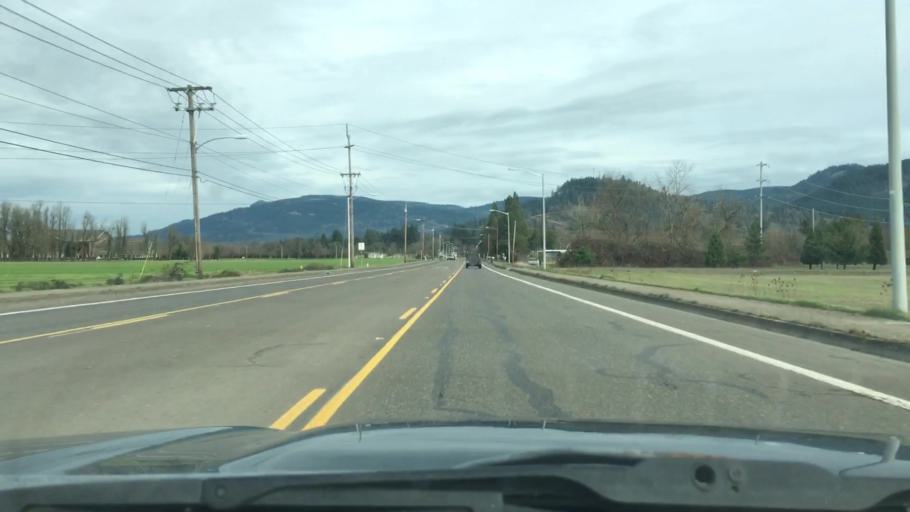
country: US
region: Oregon
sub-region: Lane County
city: Coburg
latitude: 44.0982
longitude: -123.0654
